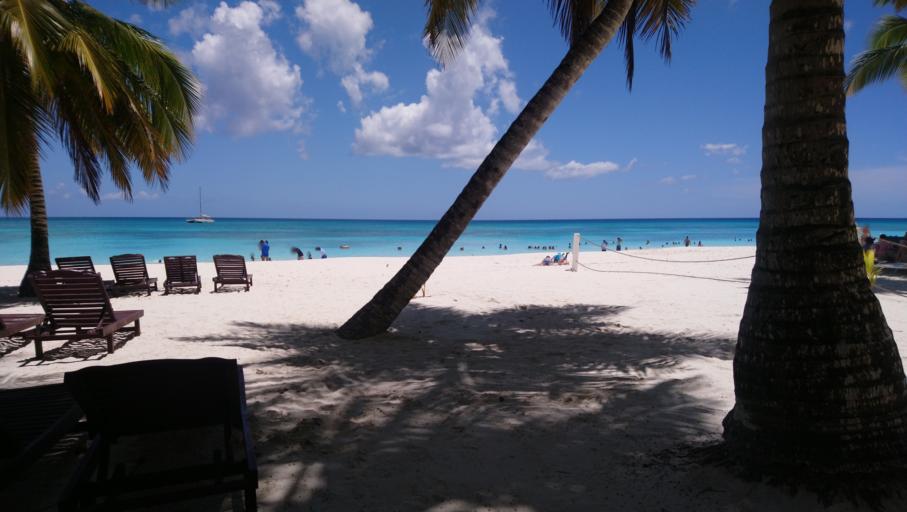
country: DO
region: La Altagracia
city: Boca de Yuma
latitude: 18.1719
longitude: -68.7815
